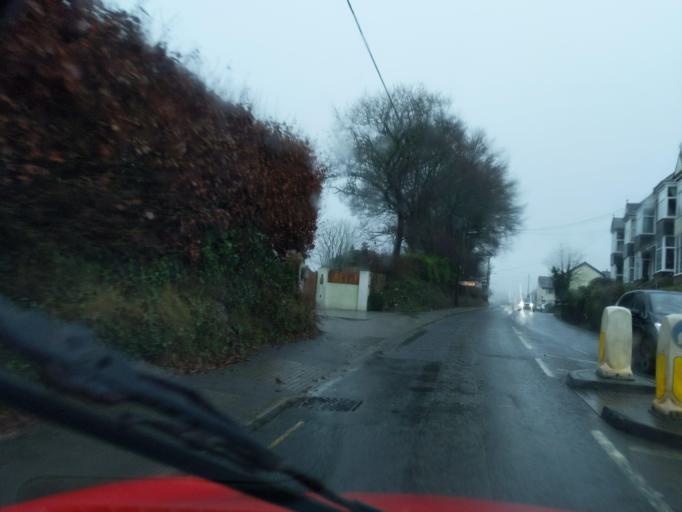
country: GB
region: England
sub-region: Cornwall
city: Callington
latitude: 50.5067
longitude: -4.3134
